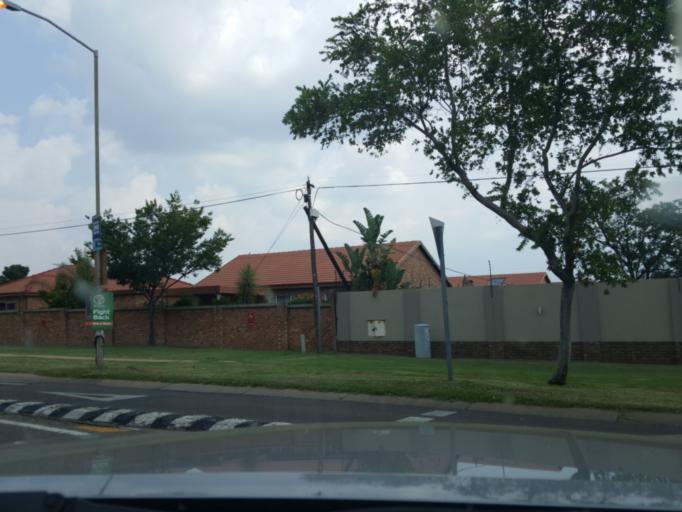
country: ZA
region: Gauteng
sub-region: City of Tshwane Metropolitan Municipality
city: Centurion
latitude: -25.8398
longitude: 28.2627
